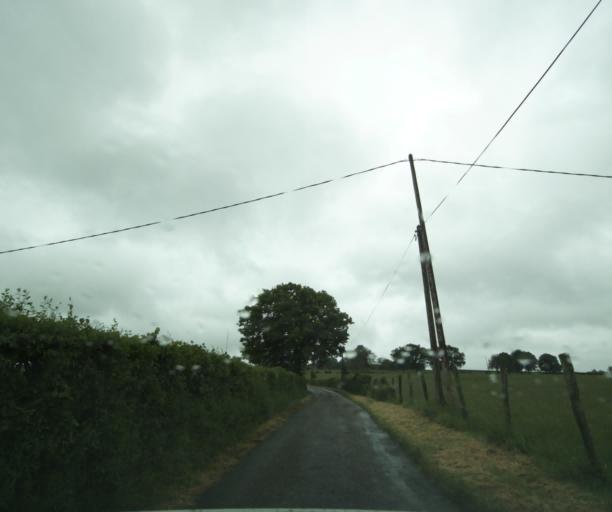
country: FR
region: Bourgogne
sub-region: Departement de Saone-et-Loire
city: Charolles
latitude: 46.4859
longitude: 4.4120
